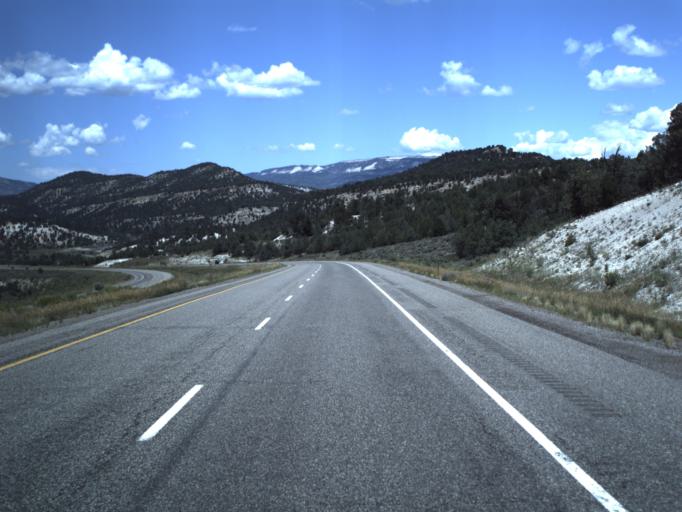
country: US
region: Utah
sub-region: Sevier County
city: Salina
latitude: 38.8631
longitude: -111.5523
